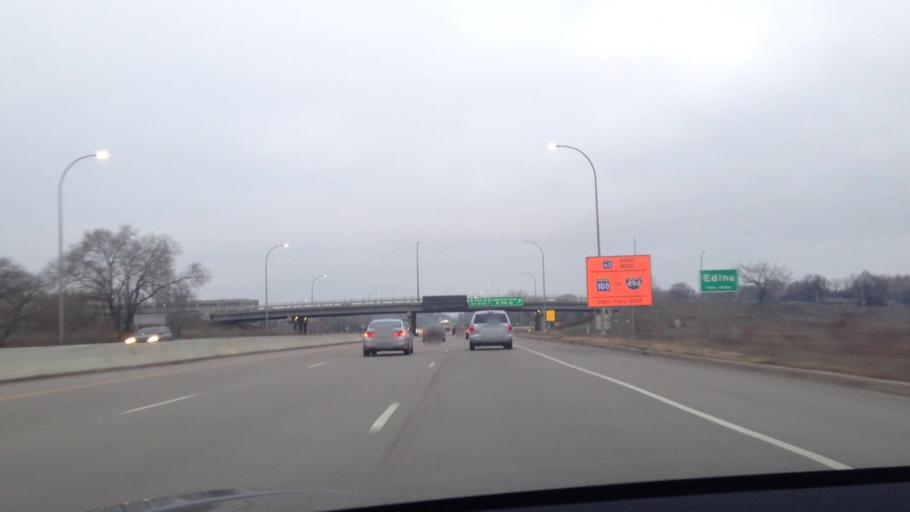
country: US
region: Minnesota
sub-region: Hennepin County
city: Edina
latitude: 44.8623
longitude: -93.3501
